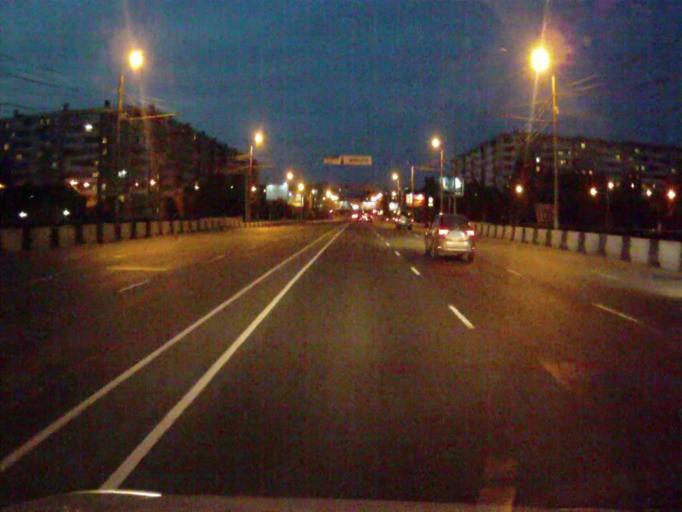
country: RU
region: Chelyabinsk
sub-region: Gorod Chelyabinsk
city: Chelyabinsk
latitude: 55.1744
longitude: 61.3582
